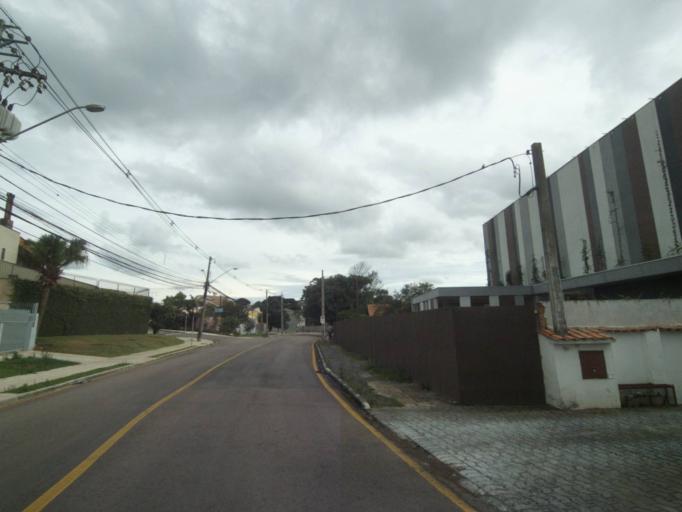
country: BR
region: Parana
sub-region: Curitiba
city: Curitiba
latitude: -25.4433
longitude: -49.3118
